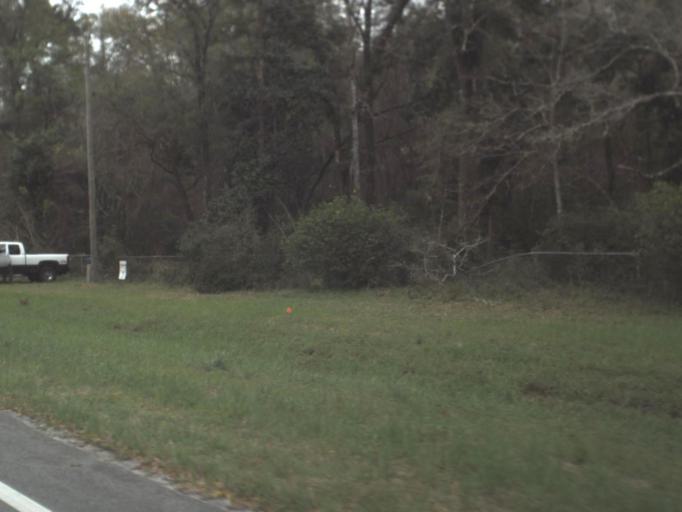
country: US
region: Florida
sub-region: Wakulla County
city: Crawfordville
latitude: 30.1471
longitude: -84.2904
